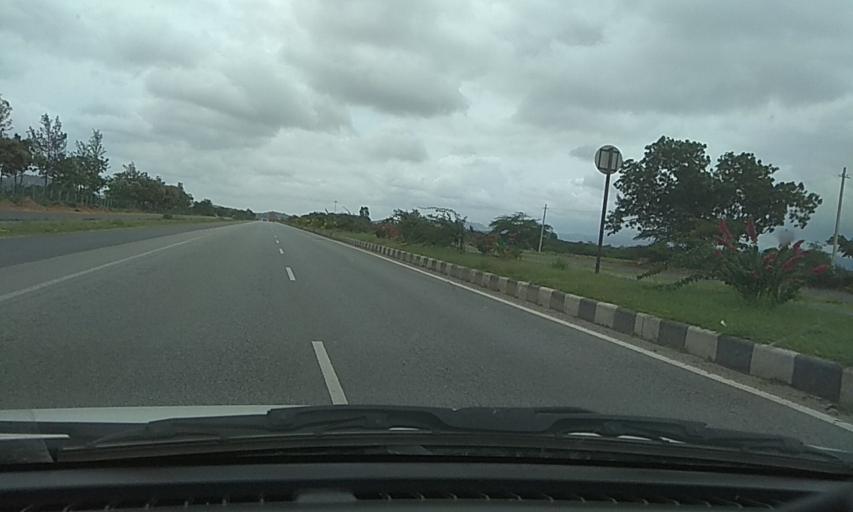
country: IN
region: Karnataka
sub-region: Chitradurga
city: Chitradurga
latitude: 14.2717
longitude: 76.3260
